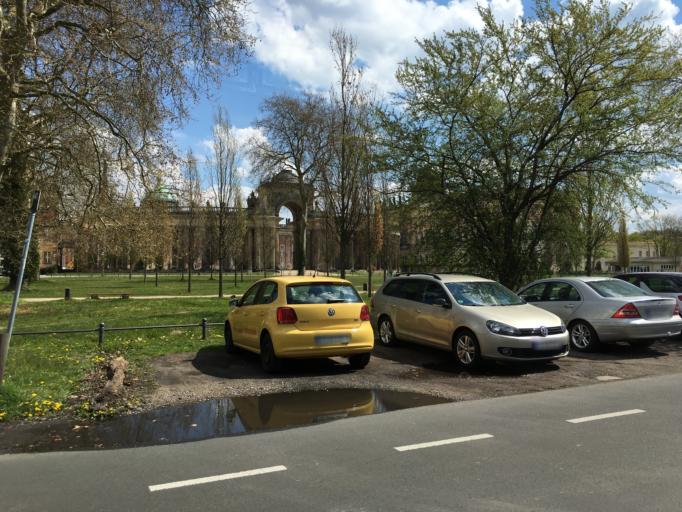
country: DE
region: Brandenburg
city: Potsdam
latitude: 52.4016
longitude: 13.0109
